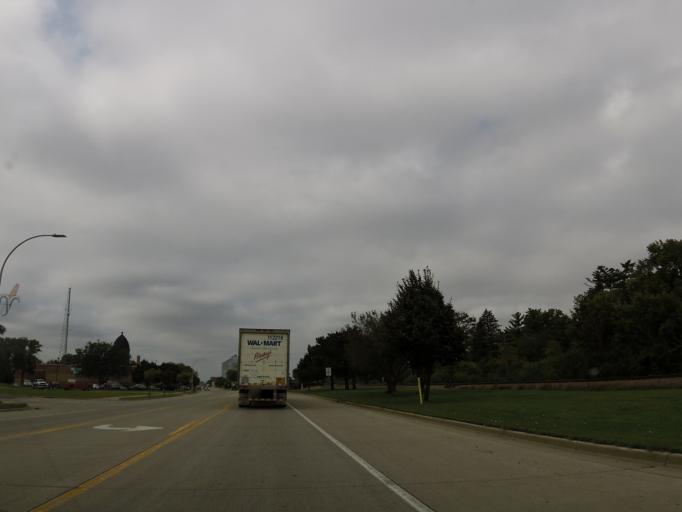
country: US
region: Minnesota
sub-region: Renville County
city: Olivia
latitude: 44.7765
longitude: -94.9791
